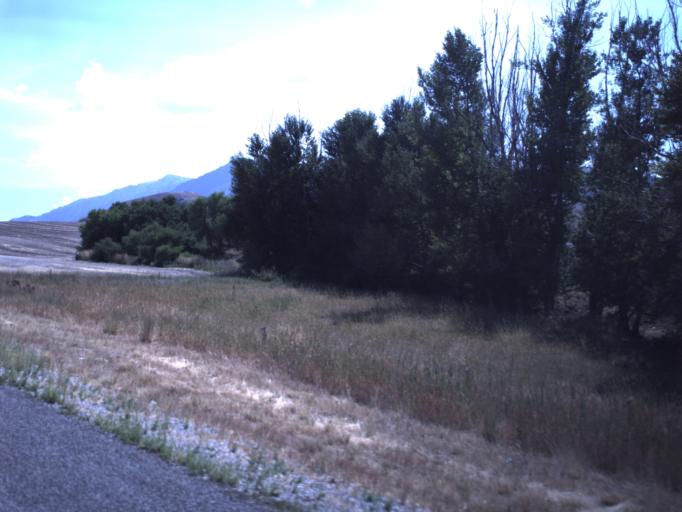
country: US
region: Utah
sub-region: Cache County
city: Mendon
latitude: 41.7835
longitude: -112.0255
